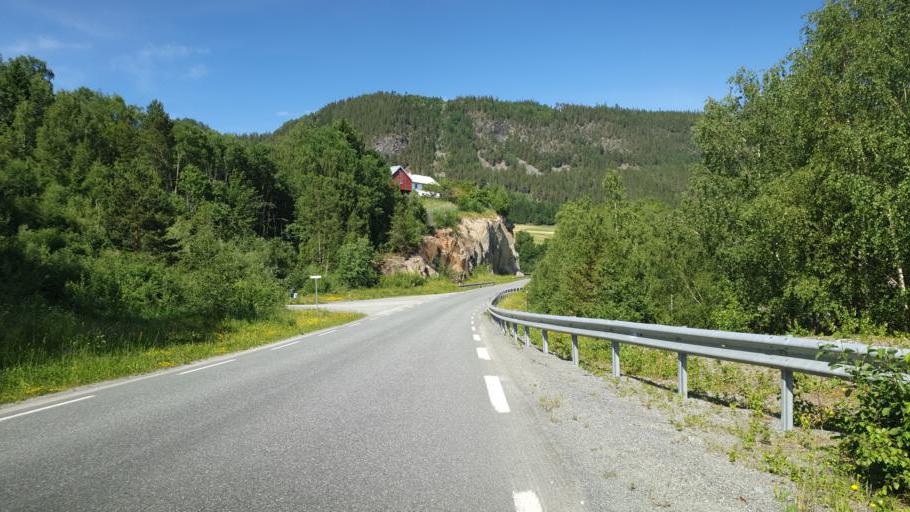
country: NO
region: Nord-Trondelag
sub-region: Leksvik
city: Leksvik
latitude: 63.6214
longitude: 10.5287
